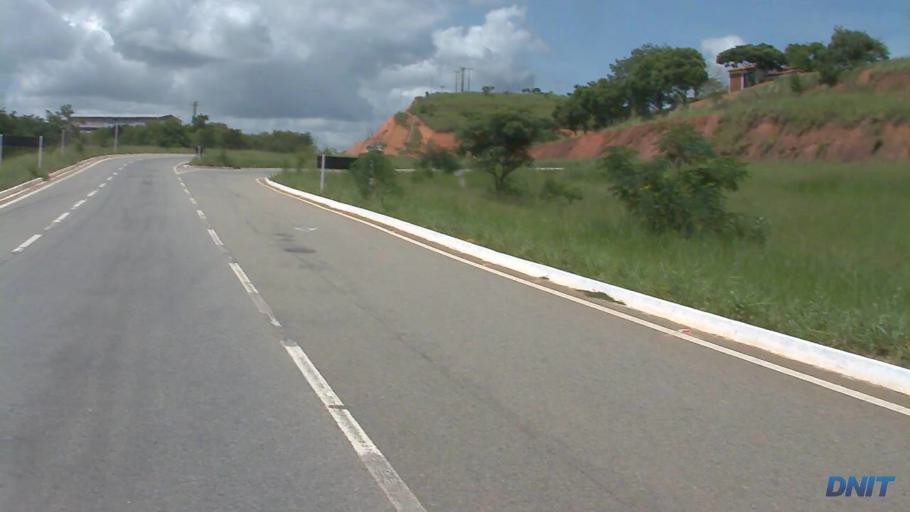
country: BR
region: Minas Gerais
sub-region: Governador Valadares
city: Governador Valadares
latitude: -18.9135
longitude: -42.0097
